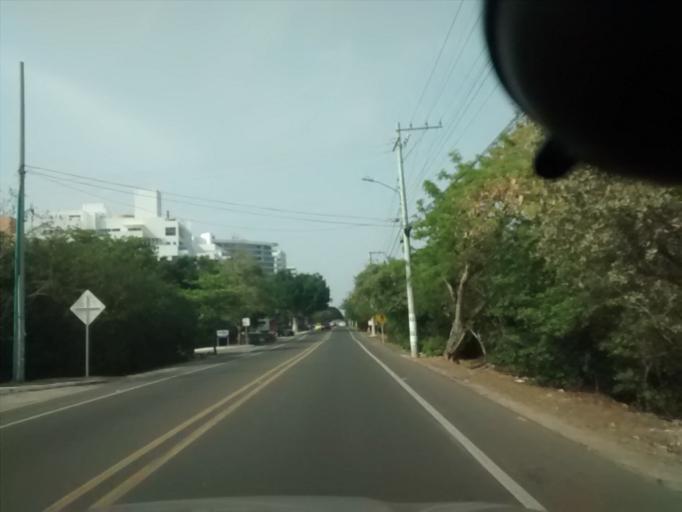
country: CO
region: Bolivar
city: Cartagena
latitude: 10.4615
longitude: -75.5044
